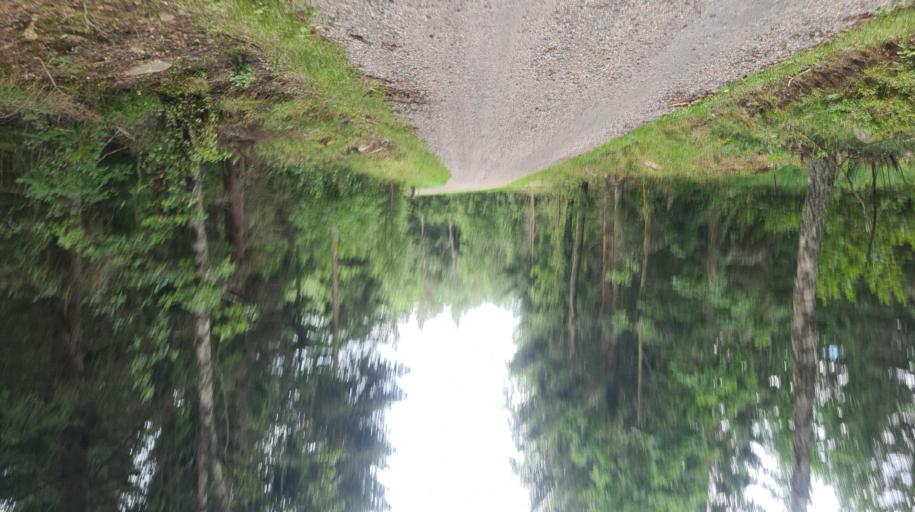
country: SE
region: Kronoberg
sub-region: Ljungby Kommun
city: Ljungby
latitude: 56.8189
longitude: 13.8619
